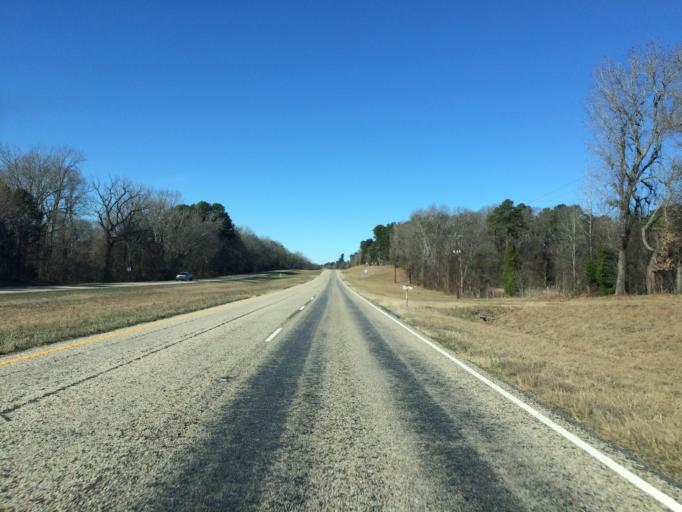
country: US
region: Texas
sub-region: Wood County
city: Mineola
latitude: 32.6454
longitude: -95.4047
